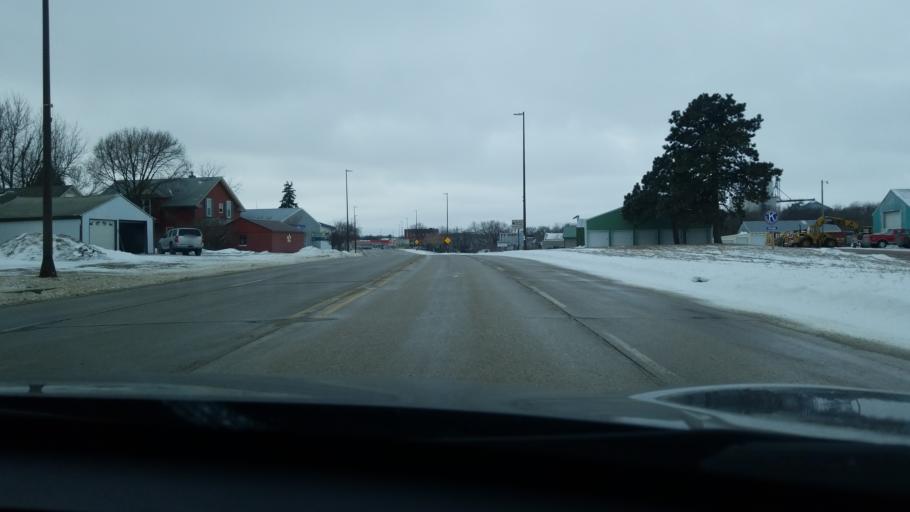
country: US
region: Iowa
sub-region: Lyon County
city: Rock Rapids
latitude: 43.4329
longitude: -96.1607
